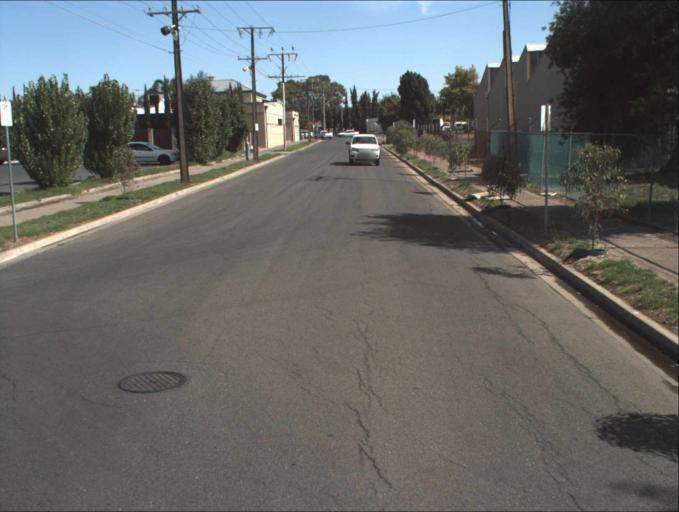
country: AU
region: South Australia
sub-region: Port Adelaide Enfield
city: Klemzig
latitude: -34.8664
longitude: 138.6457
